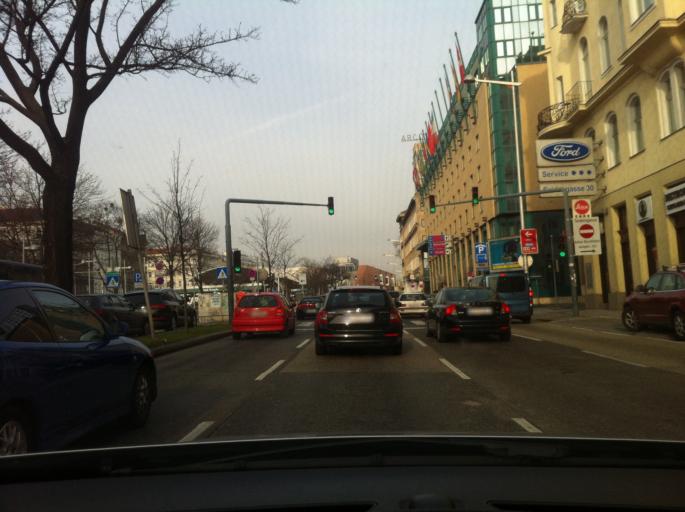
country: AT
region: Vienna
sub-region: Wien Stadt
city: Vienna
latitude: 48.1998
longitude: 16.3385
